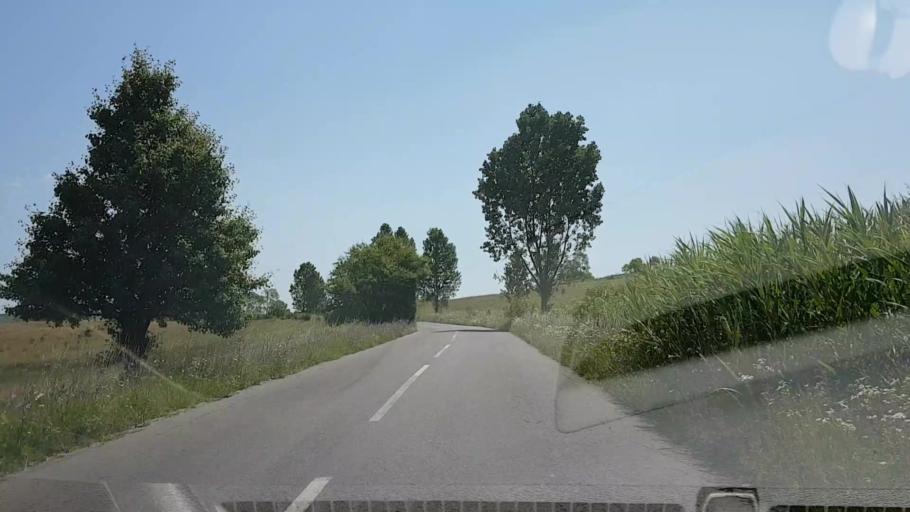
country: RO
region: Sibiu
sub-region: Comuna Merghindeal
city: Merghindeal
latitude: 45.9567
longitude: 24.7667
